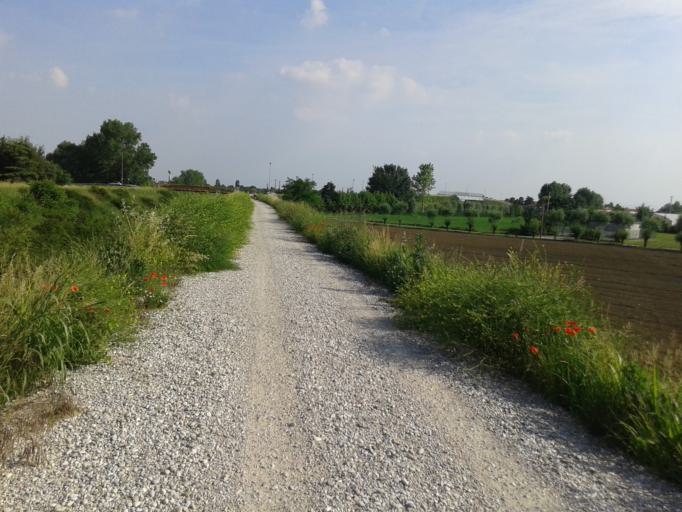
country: IT
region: Veneto
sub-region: Provincia di Padova
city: Loreggiola
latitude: 45.6157
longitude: 11.9282
